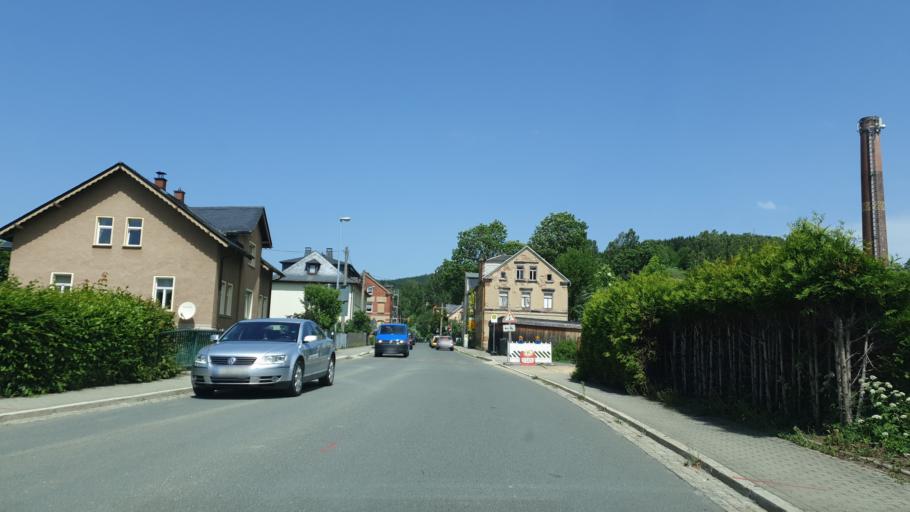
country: DE
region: Saxony
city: Klingenthal
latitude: 50.3715
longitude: 12.4698
